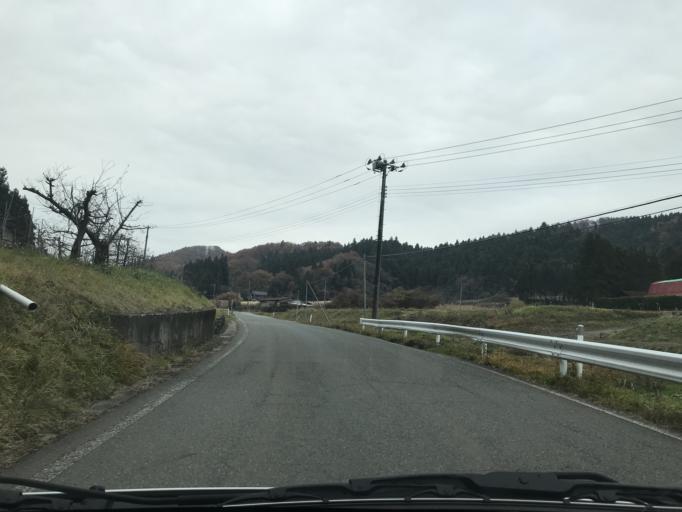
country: JP
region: Iwate
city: Kitakami
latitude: 39.2818
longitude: 141.1764
